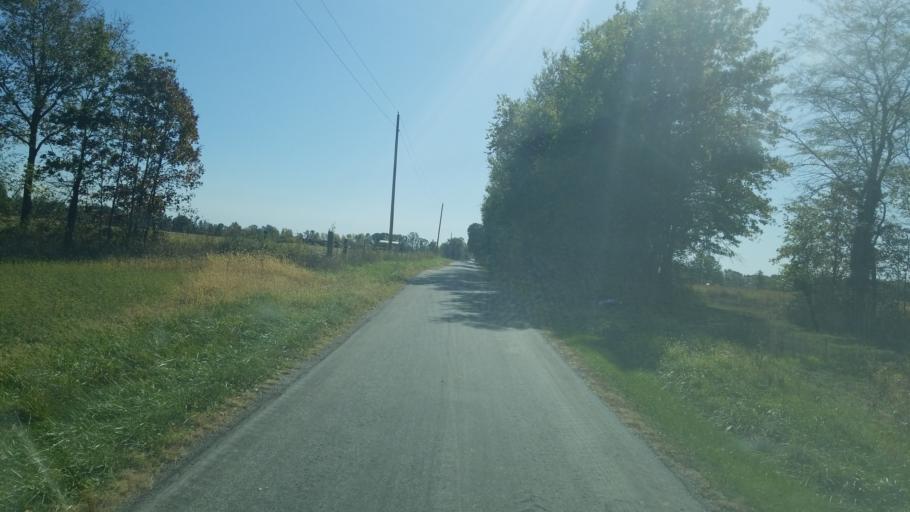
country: US
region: Ohio
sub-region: Hardin County
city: Kenton
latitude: 40.5867
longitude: -83.4216
